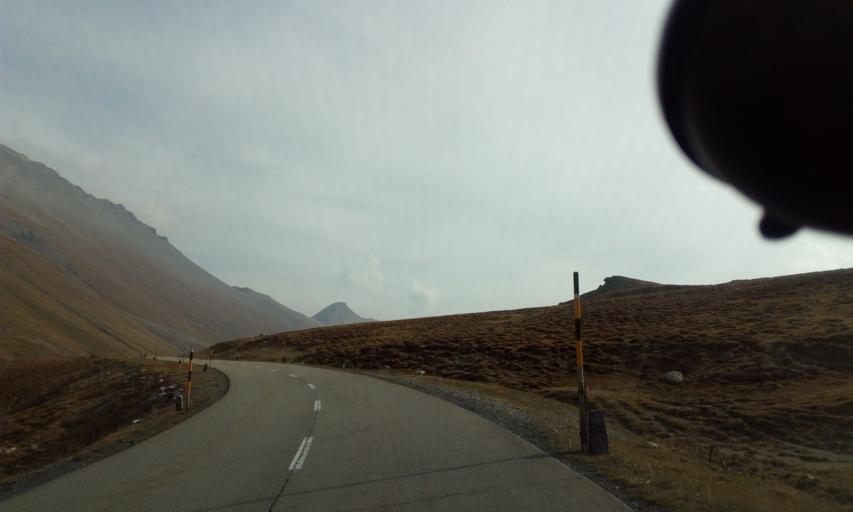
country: CH
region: Grisons
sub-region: Maloja District
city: Samedan
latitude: 46.5857
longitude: 9.8542
